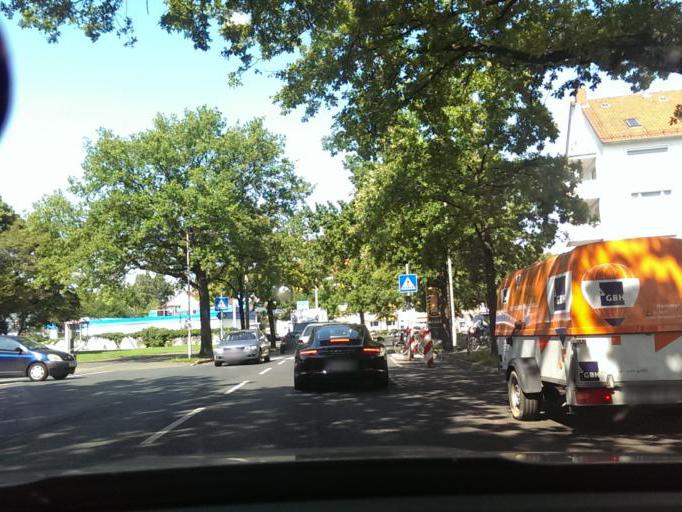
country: DE
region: Lower Saxony
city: Hannover
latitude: 52.3975
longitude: 9.7422
